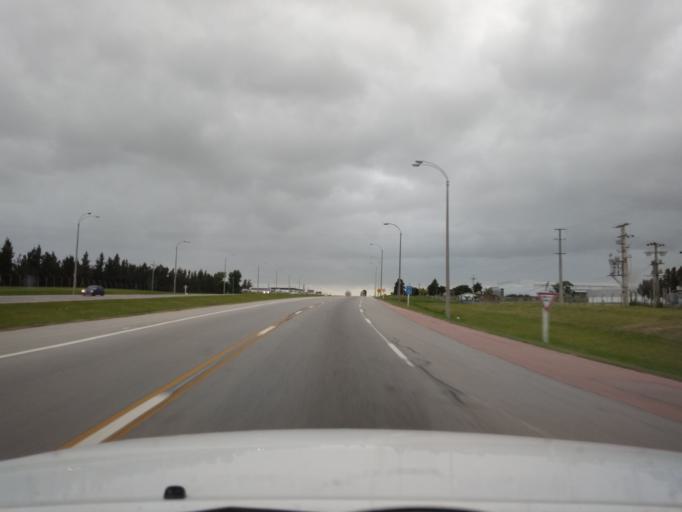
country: UY
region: Canelones
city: Las Piedras
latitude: -34.6967
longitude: -56.2386
